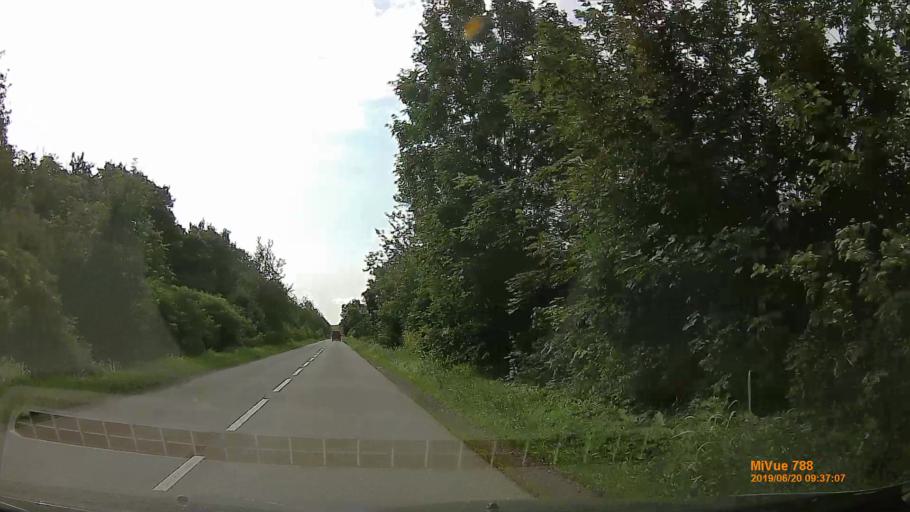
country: HU
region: Baranya
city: Pecsvarad
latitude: 46.1663
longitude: 18.4607
